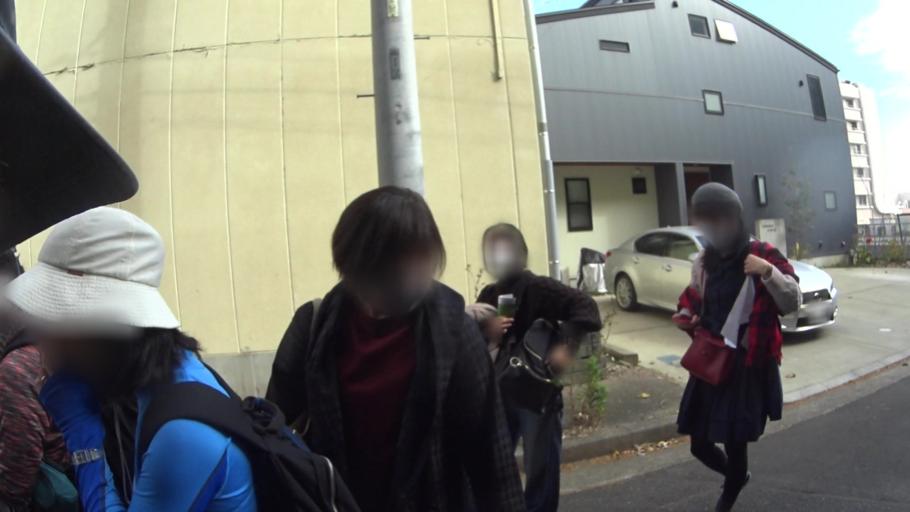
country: JP
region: Ibaraki
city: Mito-shi
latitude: 36.3720
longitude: 140.4853
